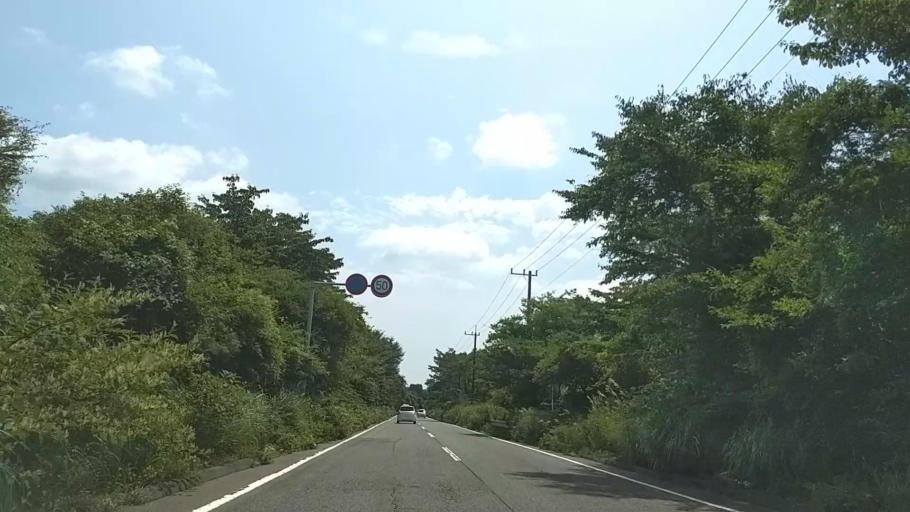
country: JP
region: Shizuoka
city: Fujinomiya
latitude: 35.3666
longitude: 138.5769
